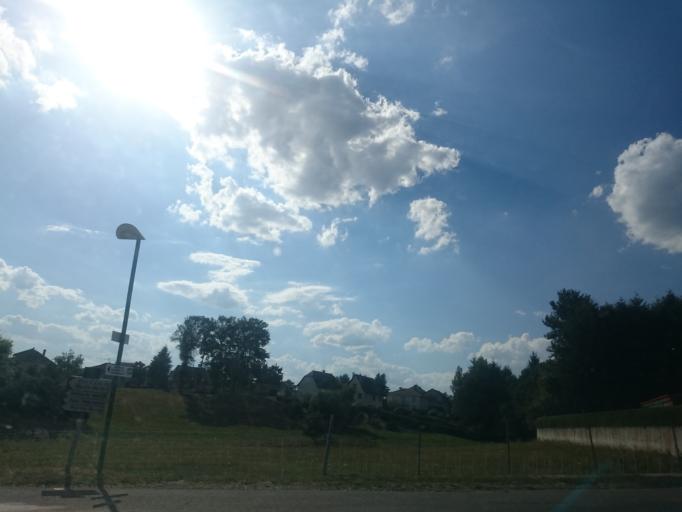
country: FR
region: Auvergne
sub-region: Departement du Cantal
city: Saint-Mamet-la-Salvetat
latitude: 44.8536
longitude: 2.2320
